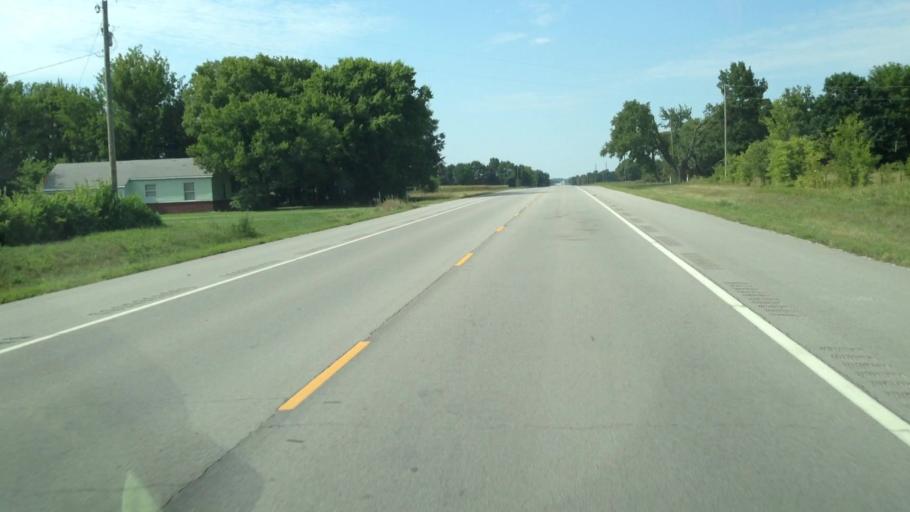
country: US
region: Kansas
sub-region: Labette County
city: Altamont
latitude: 37.2547
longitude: -95.2671
